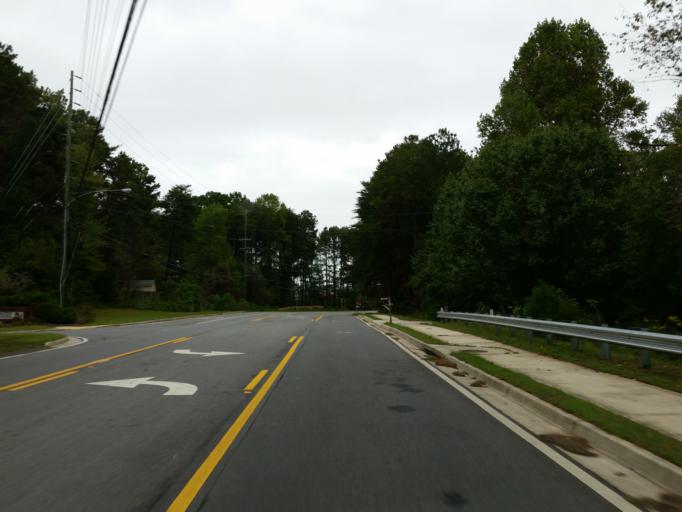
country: US
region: Georgia
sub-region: Cherokee County
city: Woodstock
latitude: 34.0730
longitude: -84.4897
